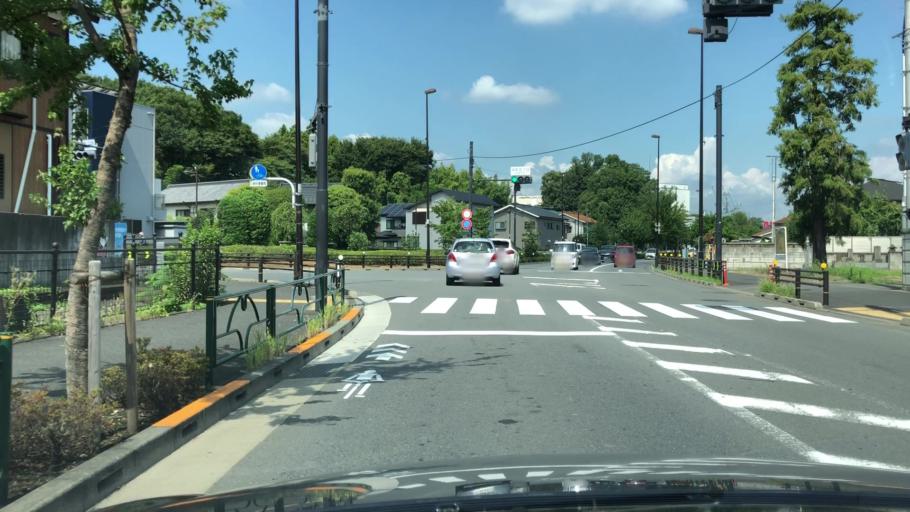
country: JP
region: Tokyo
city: Hino
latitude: 35.6852
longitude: 139.3813
